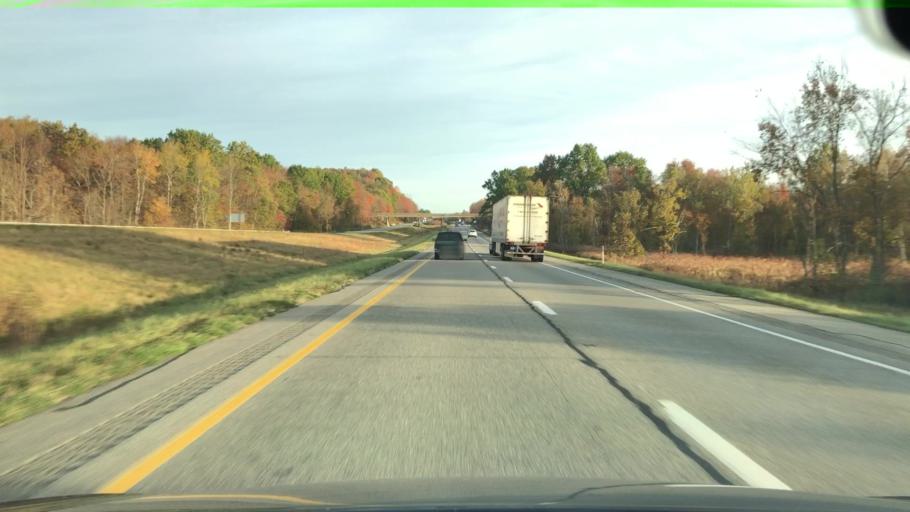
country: US
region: Pennsylvania
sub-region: Mercer County
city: Stoneboro
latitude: 41.2915
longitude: -80.1578
